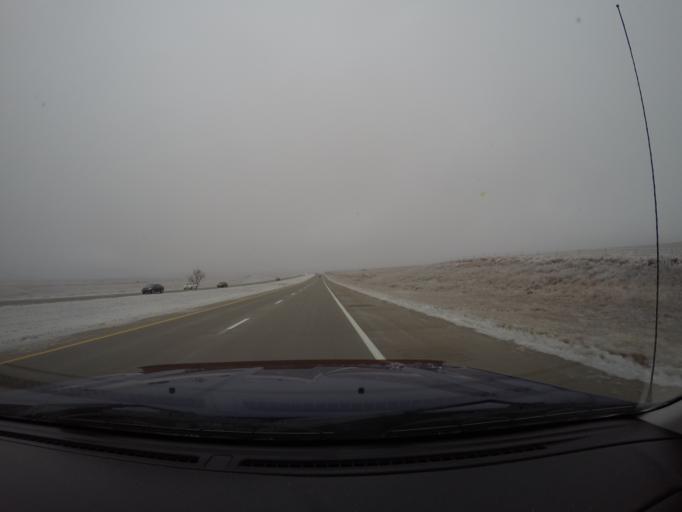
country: US
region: Kansas
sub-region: Wabaunsee County
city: Alma
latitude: 39.0655
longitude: -96.4194
